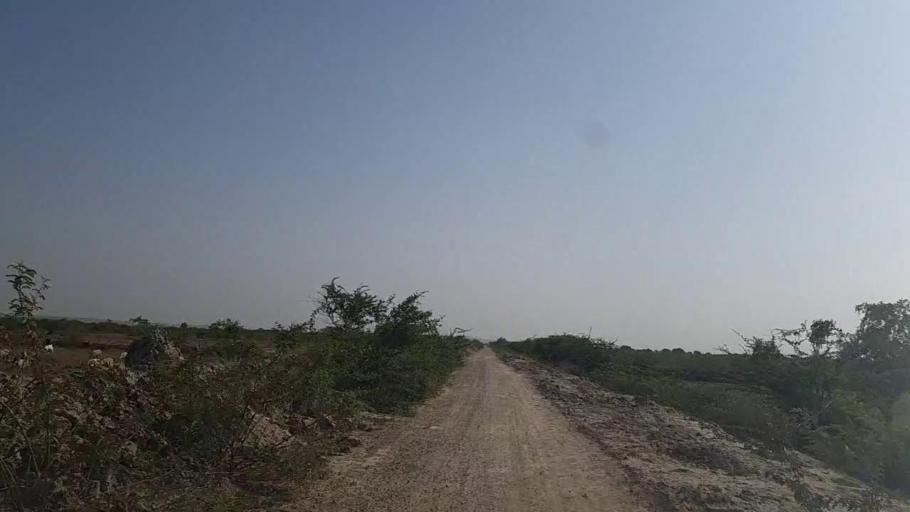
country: PK
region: Sindh
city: Kadhan
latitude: 24.5857
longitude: 69.2629
